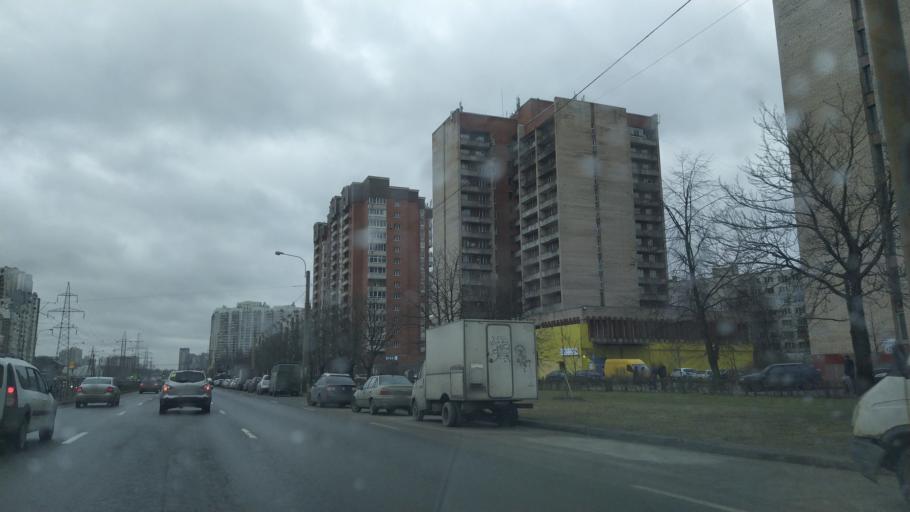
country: RU
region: St.-Petersburg
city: Komendantsky aerodrom
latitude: 60.0045
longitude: 30.2860
